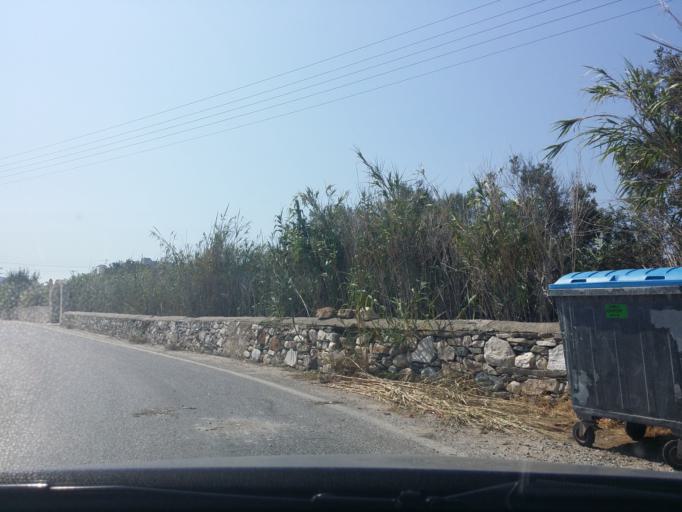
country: GR
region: South Aegean
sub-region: Nomos Kykladon
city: Antiparos
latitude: 37.0401
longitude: 25.1075
